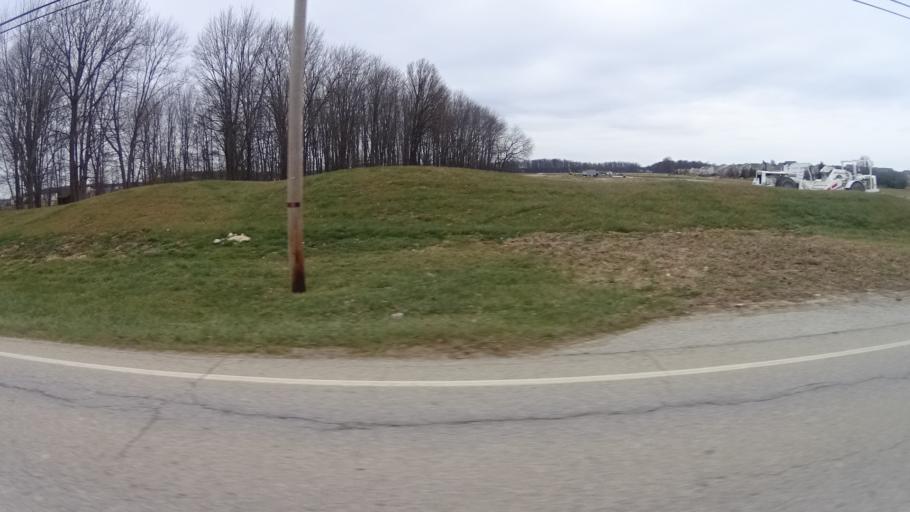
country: US
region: Ohio
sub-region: Lorain County
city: North Ridgeville
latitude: 41.3494
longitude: -82.0421
